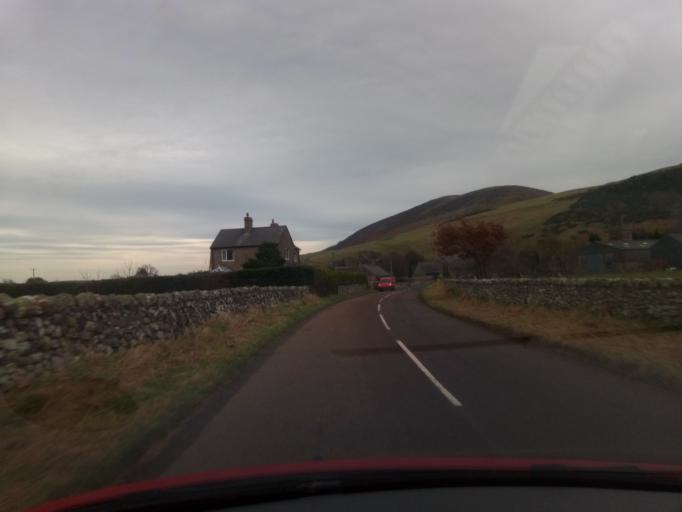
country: GB
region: England
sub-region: Northumberland
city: Kirknewton
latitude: 55.5673
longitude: -2.1412
